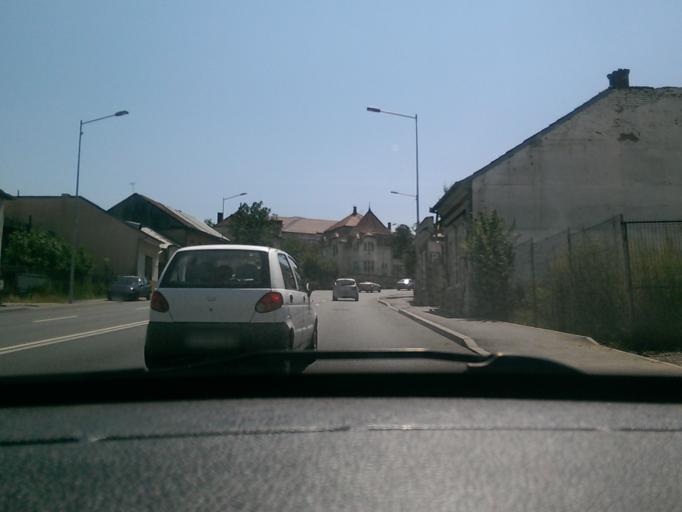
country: RO
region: Cluj
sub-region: Municipiul Cluj-Napoca
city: Cluj-Napoca
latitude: 46.7665
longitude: 23.5984
